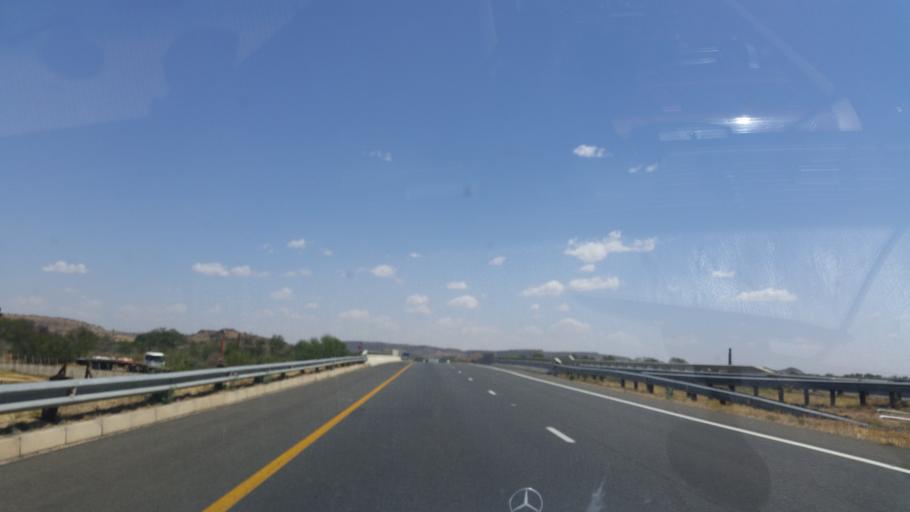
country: ZA
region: Orange Free State
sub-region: Mangaung Metropolitan Municipality
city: Bloemfontein
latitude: -28.9686
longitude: 26.3328
